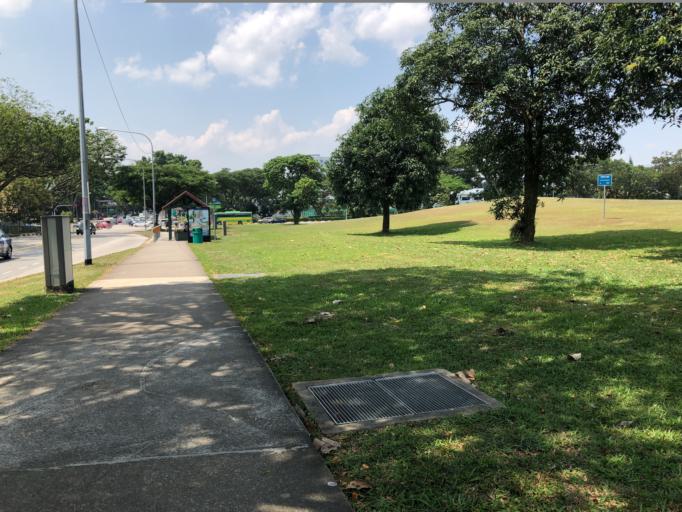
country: SG
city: Singapore
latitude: 1.3757
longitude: 103.8451
